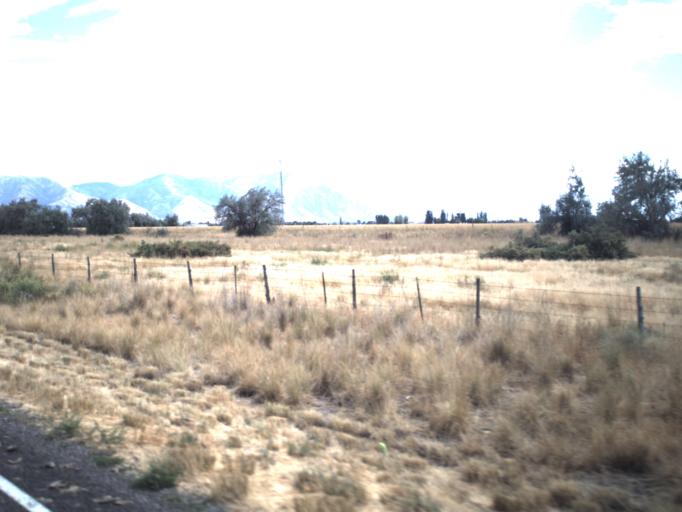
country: US
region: Utah
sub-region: Box Elder County
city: Honeyville
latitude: 41.5673
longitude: -112.1884
